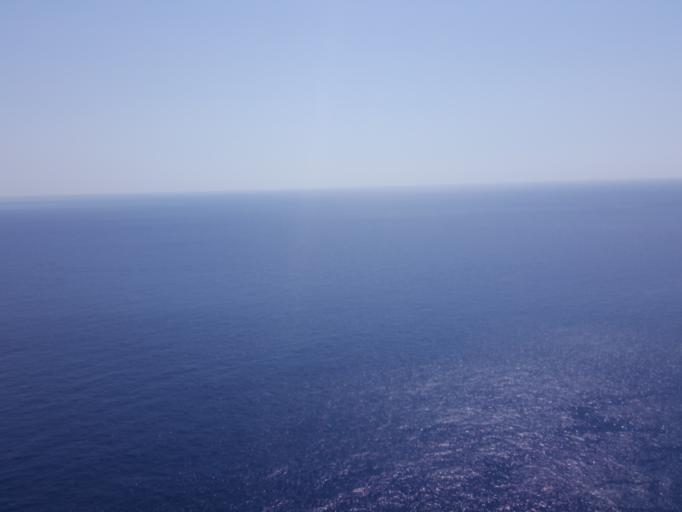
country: GR
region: South Aegean
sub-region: Nomos Dodekanisou
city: Lardos
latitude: 36.0908
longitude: 28.0880
